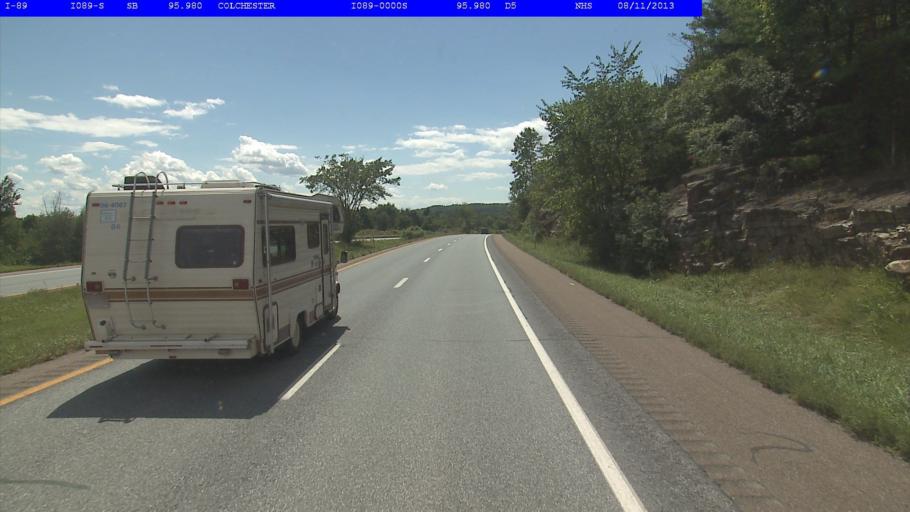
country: US
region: Vermont
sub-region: Chittenden County
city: Colchester
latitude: 44.5635
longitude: -73.1797
